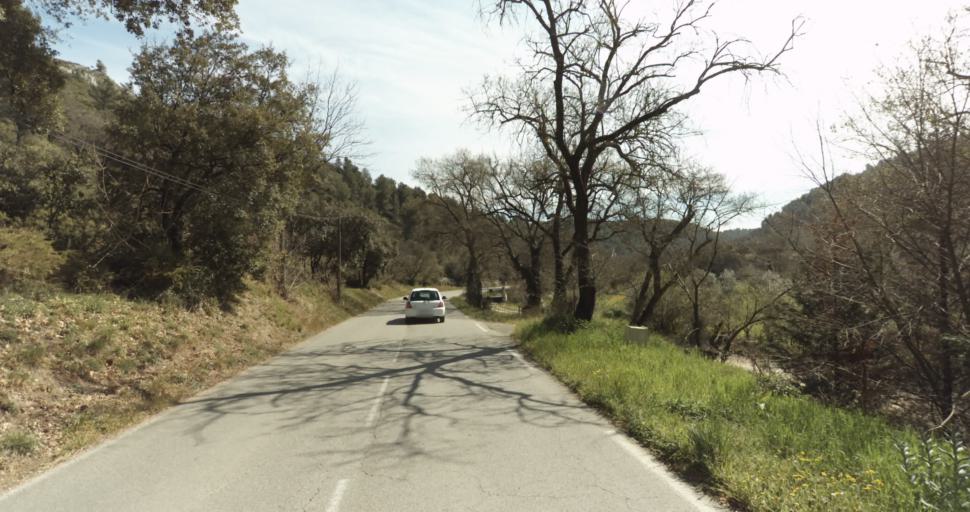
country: FR
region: Provence-Alpes-Cote d'Azur
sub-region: Departement des Bouches-du-Rhone
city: Ventabren
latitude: 43.5186
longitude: 5.3027
